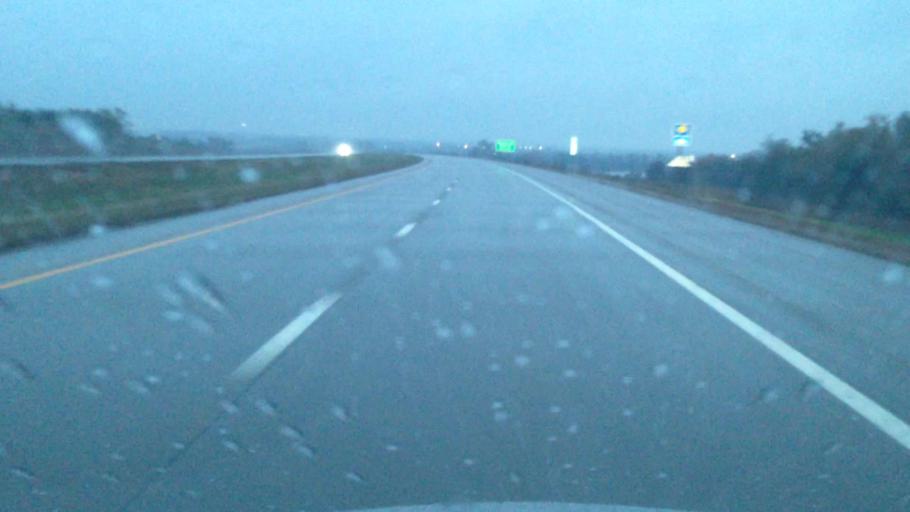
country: US
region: Kansas
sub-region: Franklin County
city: Ottawa
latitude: 38.6773
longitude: -95.2626
